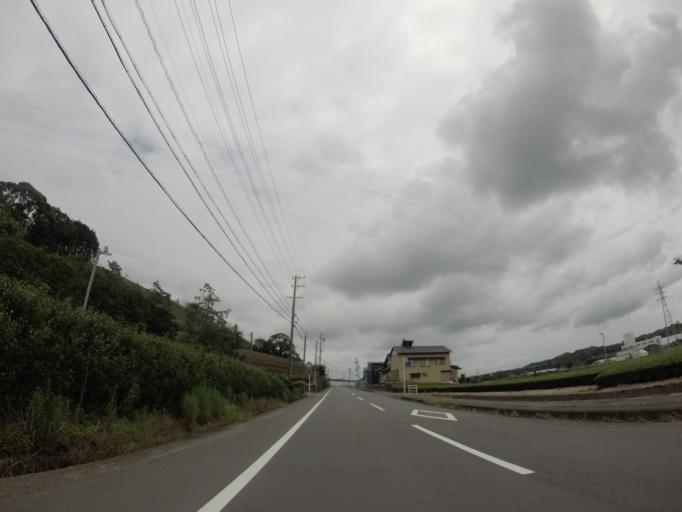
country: JP
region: Shizuoka
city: Shimada
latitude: 34.7644
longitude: 138.1948
